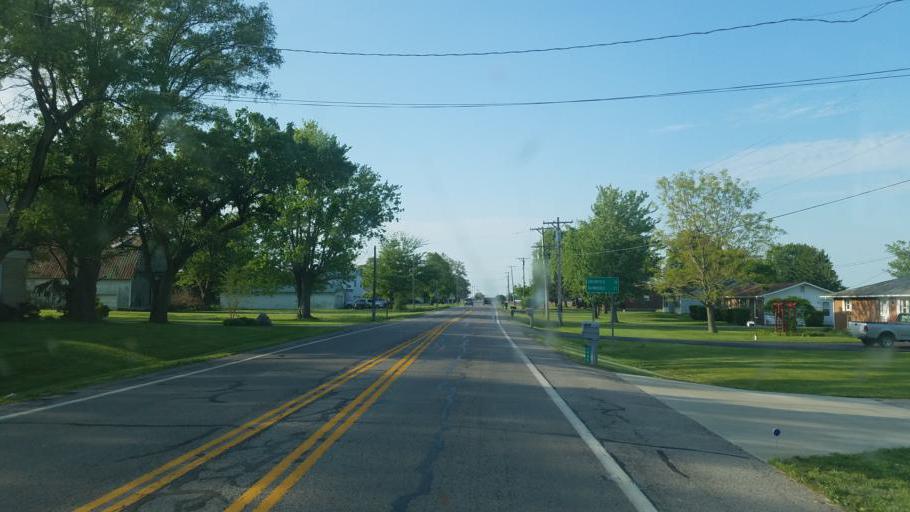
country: US
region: Ohio
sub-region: Fayette County
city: Washington Court House
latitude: 39.5122
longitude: -83.4421
